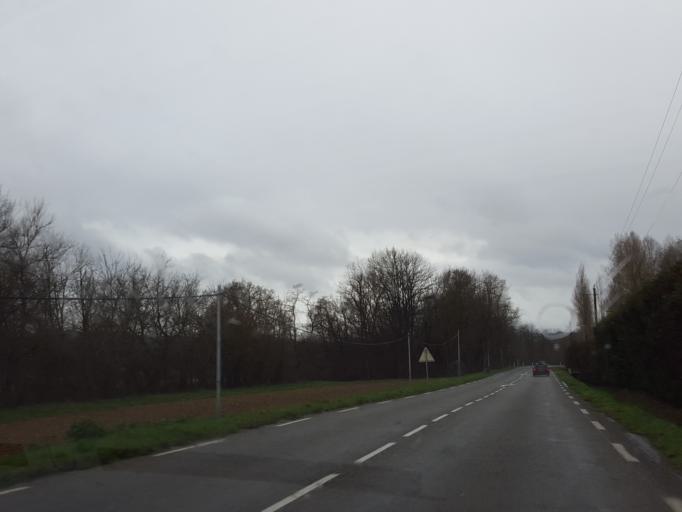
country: FR
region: Midi-Pyrenees
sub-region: Departement de l'Ariege
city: Mirepoix
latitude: 43.0980
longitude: 1.8991
